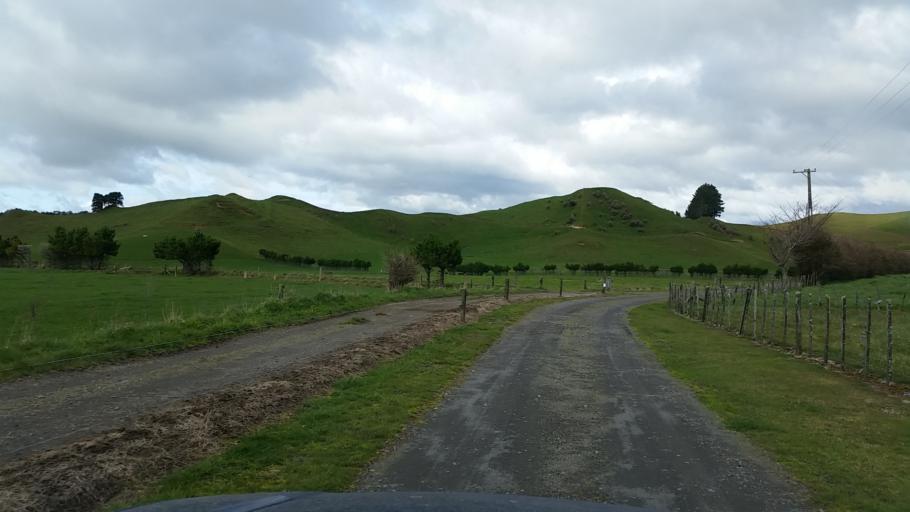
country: NZ
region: Taranaki
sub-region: South Taranaki District
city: Eltham
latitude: -39.3503
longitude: 174.3836
